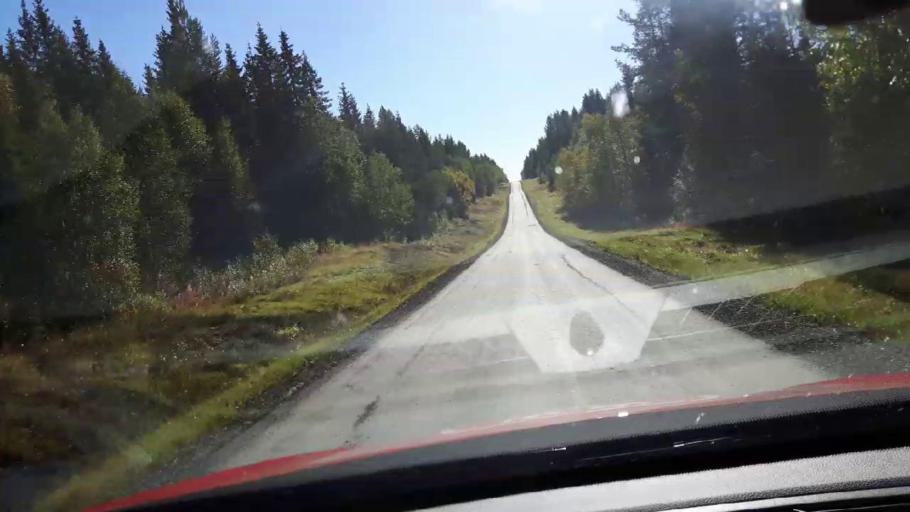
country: NO
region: Nord-Trondelag
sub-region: Lierne
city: Sandvika
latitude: 64.6088
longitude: 13.9582
